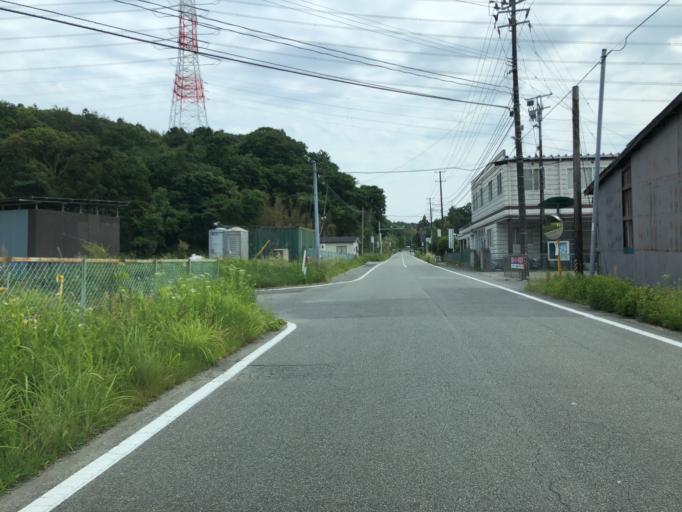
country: JP
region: Fukushima
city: Namie
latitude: 37.3177
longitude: 141.0079
